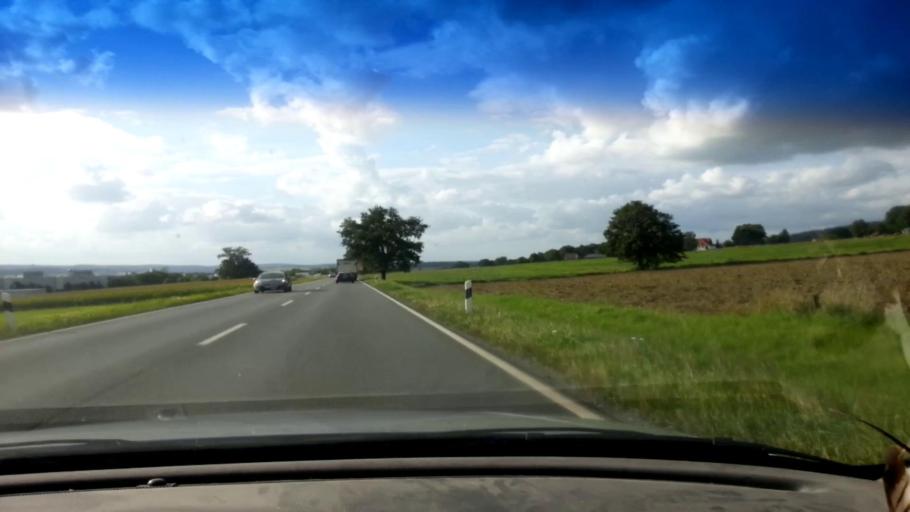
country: DE
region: Bavaria
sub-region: Upper Franconia
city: Himmelkron
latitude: 50.0521
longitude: 11.6330
